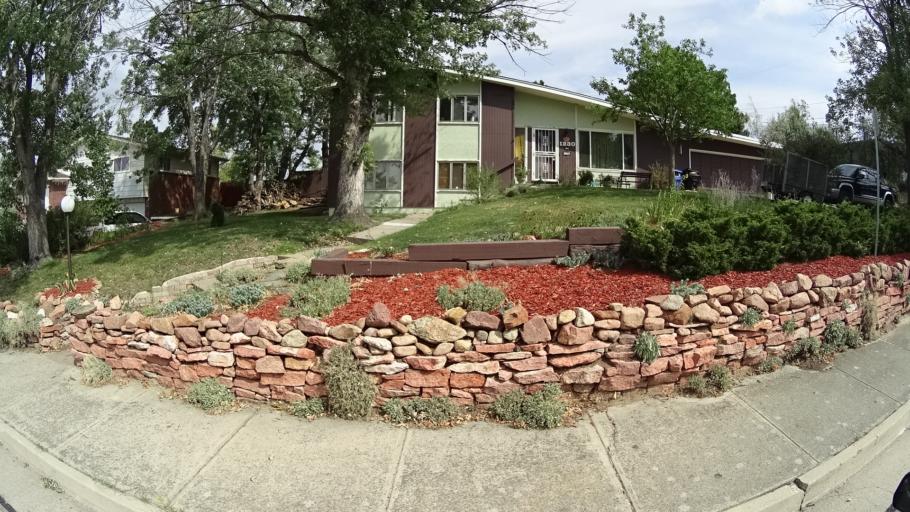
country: US
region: Colorado
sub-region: El Paso County
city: Colorado Springs
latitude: 38.8900
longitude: -104.8012
